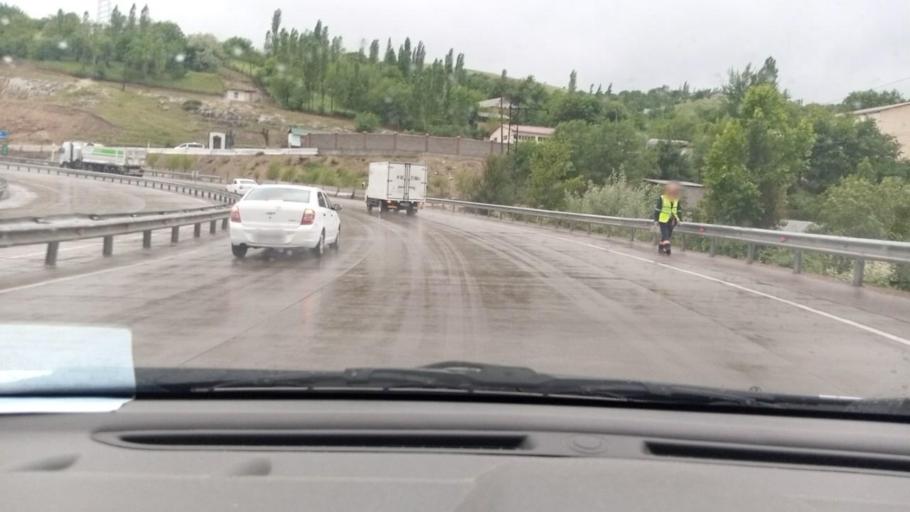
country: UZ
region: Toshkent
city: Angren
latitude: 41.0752
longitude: 70.2531
